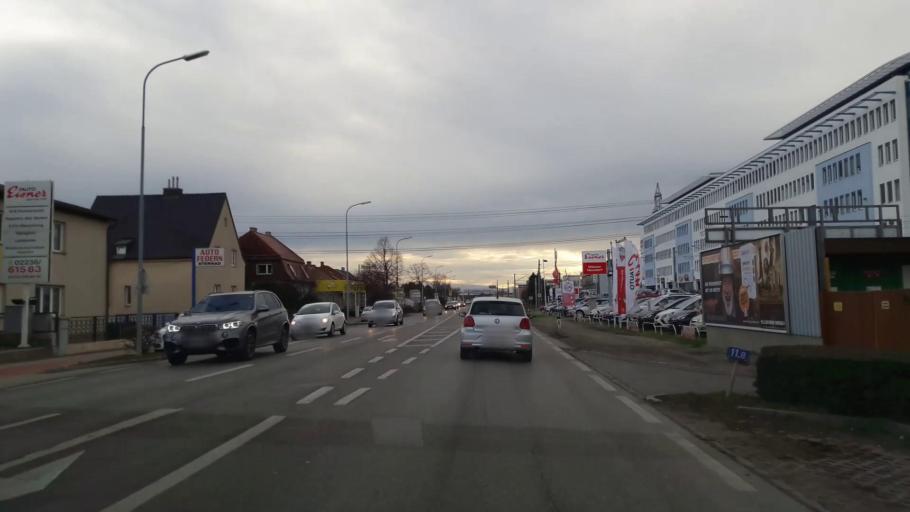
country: AT
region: Lower Austria
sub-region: Politischer Bezirk Modling
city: Wiener Neudorf
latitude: 48.0818
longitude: 16.3139
